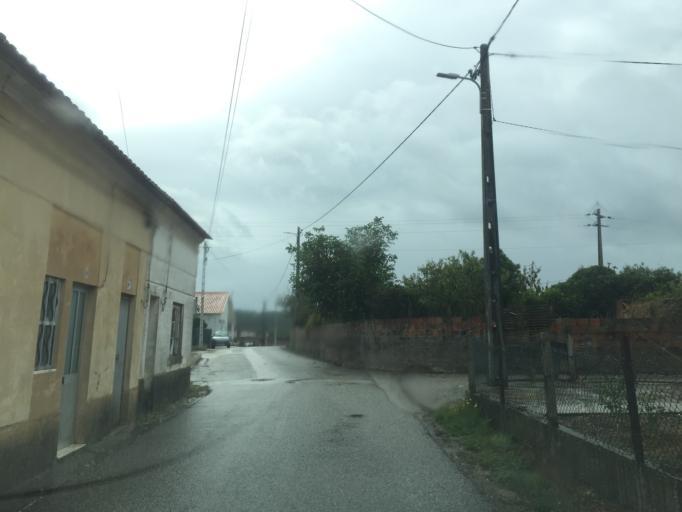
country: PT
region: Coimbra
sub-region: Figueira da Foz
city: Lavos
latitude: 40.0610
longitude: -8.7710
